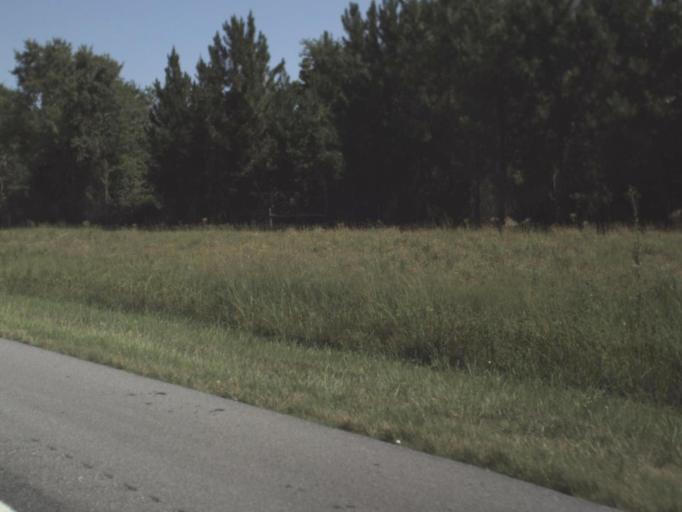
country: US
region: Florida
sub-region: Suwannee County
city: Live Oak
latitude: 30.3367
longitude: -82.9706
